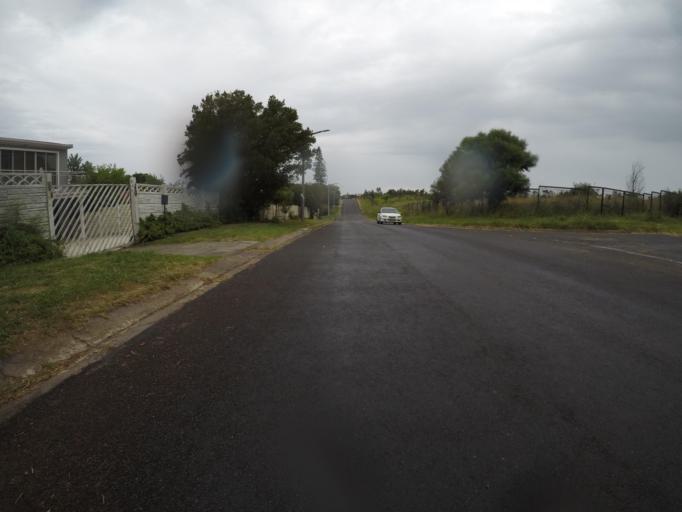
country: ZA
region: Eastern Cape
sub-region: Buffalo City Metropolitan Municipality
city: East London
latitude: -32.9902
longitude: 27.8491
